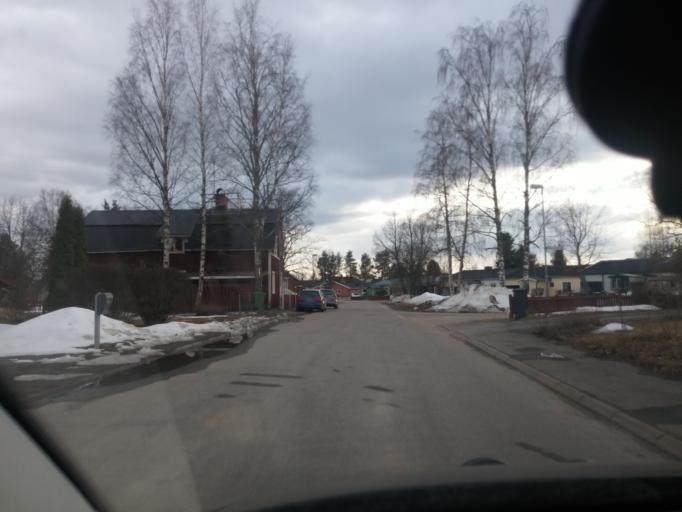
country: SE
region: Gaevleborg
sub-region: Ljusdals Kommun
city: Ljusdal
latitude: 61.8336
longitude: 16.0980
